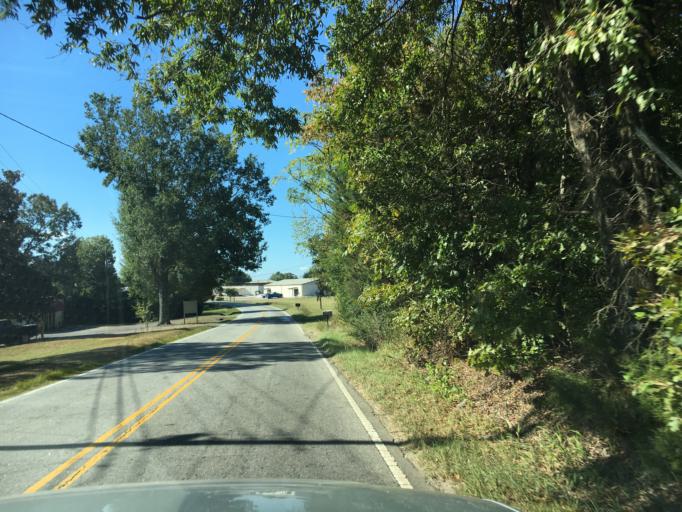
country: US
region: South Carolina
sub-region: Spartanburg County
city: Duncan
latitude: 34.8859
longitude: -82.1490
